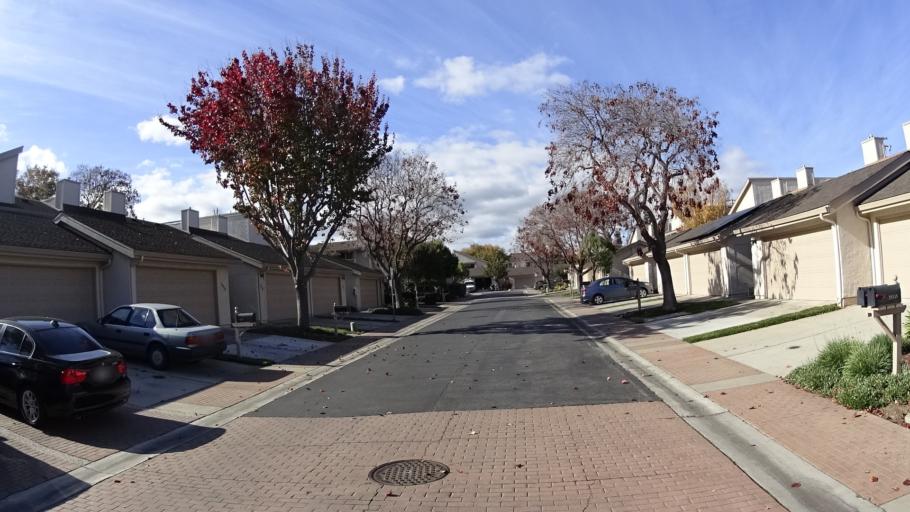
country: US
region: California
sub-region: Santa Clara County
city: Cupertino
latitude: 37.3391
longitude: -122.0333
